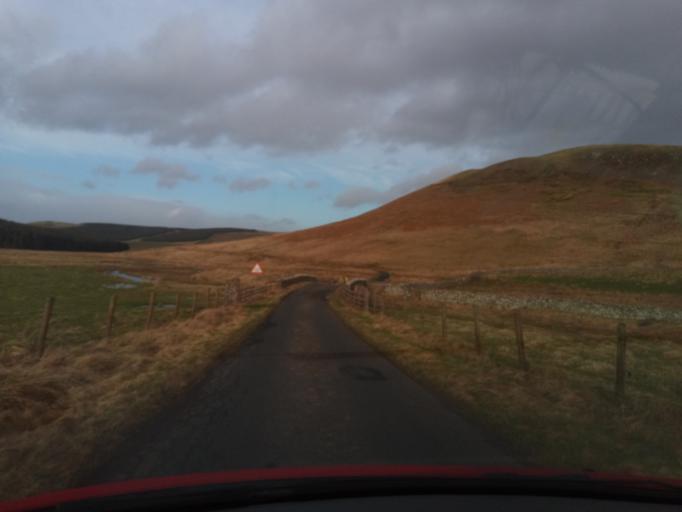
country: GB
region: Scotland
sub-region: The Scottish Borders
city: Jedburgh
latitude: 55.4194
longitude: -2.4156
